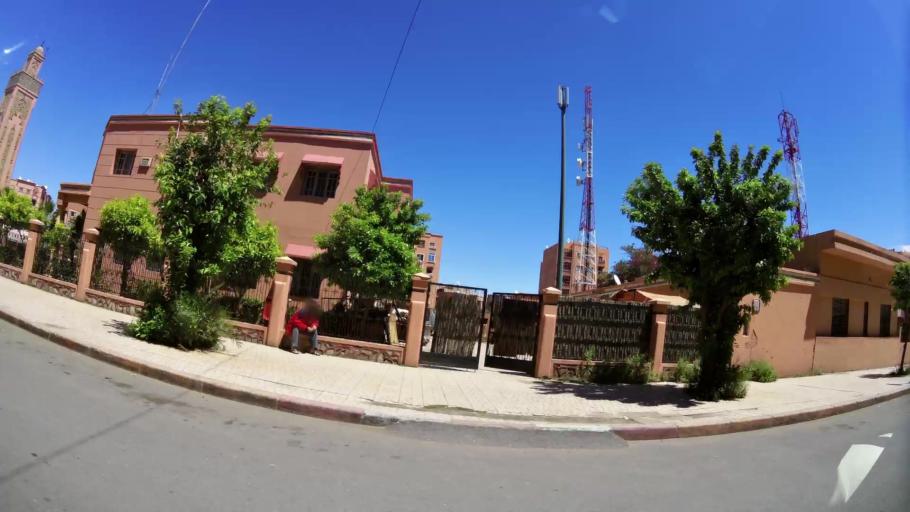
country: MA
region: Marrakech-Tensift-Al Haouz
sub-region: Marrakech
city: Marrakesh
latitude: 31.6333
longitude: -8.0551
